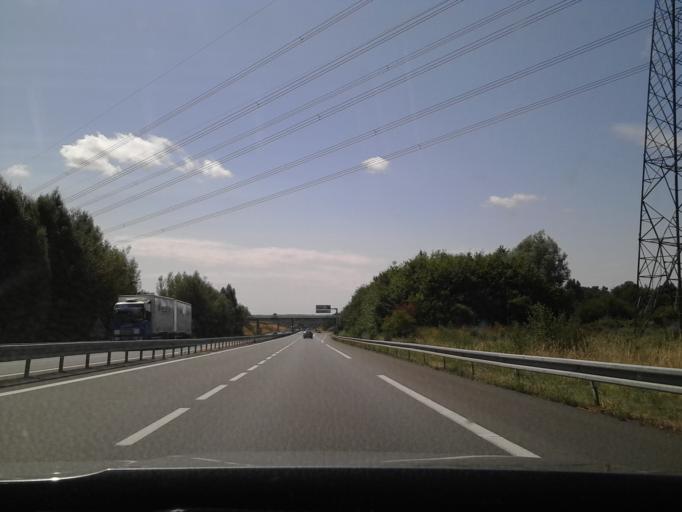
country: FR
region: Pays de la Loire
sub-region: Departement de la Sarthe
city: Ecommoy
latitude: 47.8261
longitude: 0.3065
